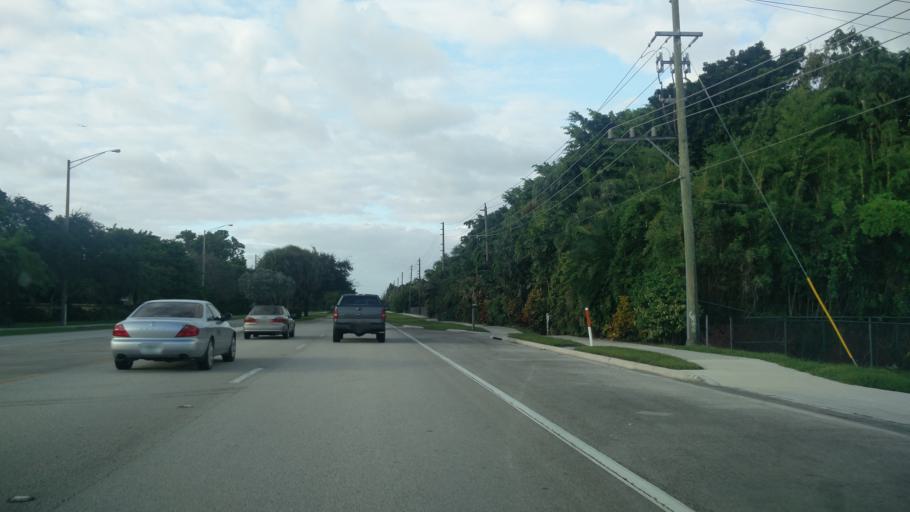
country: US
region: Florida
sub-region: Broward County
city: Cooper City
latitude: 26.0361
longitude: -80.2807
